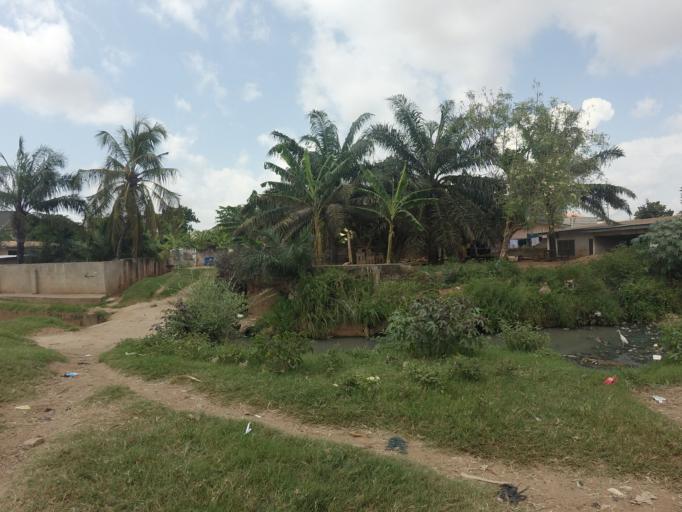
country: GH
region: Greater Accra
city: Dome
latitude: 5.6184
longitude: -0.2437
